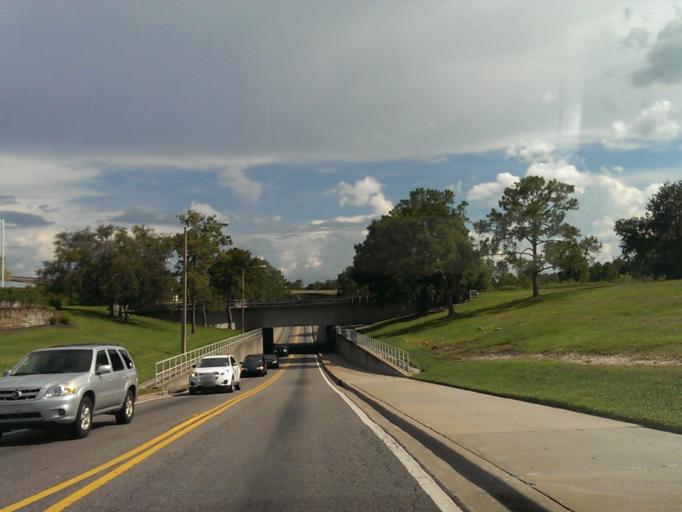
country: US
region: Florida
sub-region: Orange County
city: Bay Hill
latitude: 28.4140
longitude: -81.5765
